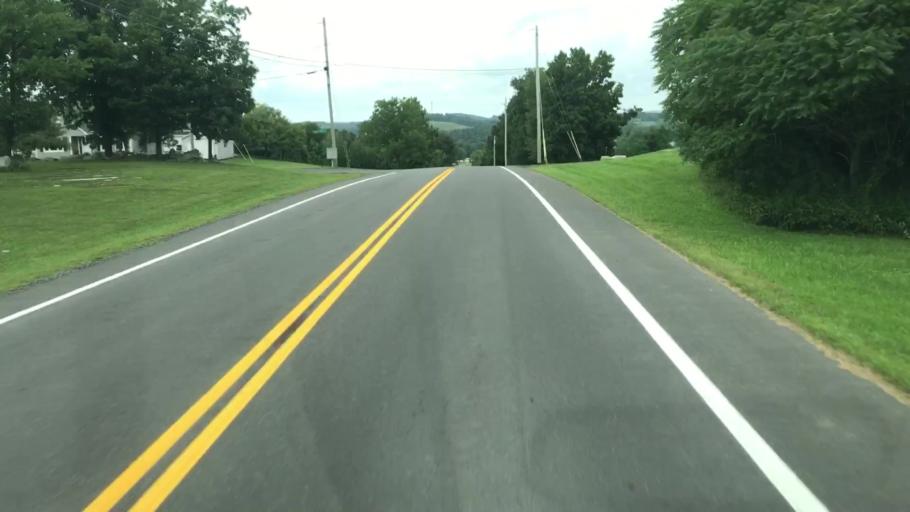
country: US
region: New York
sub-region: Onondaga County
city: Elbridge
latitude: 43.0013
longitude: -76.4399
